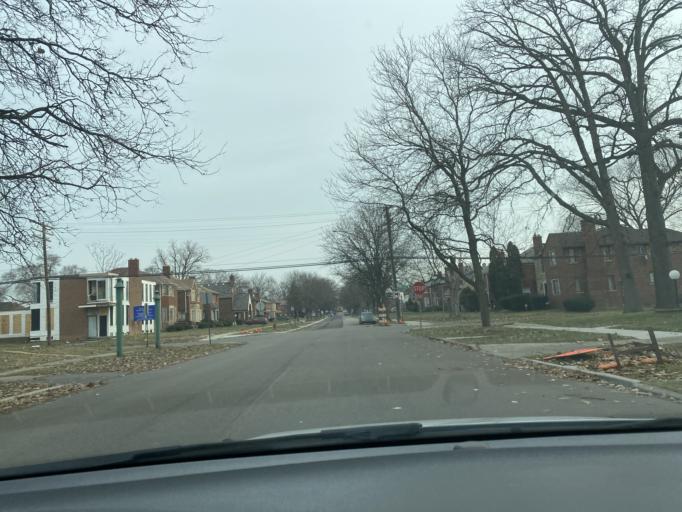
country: US
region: Michigan
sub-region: Wayne County
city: Highland Park
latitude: 42.3833
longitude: -83.1327
